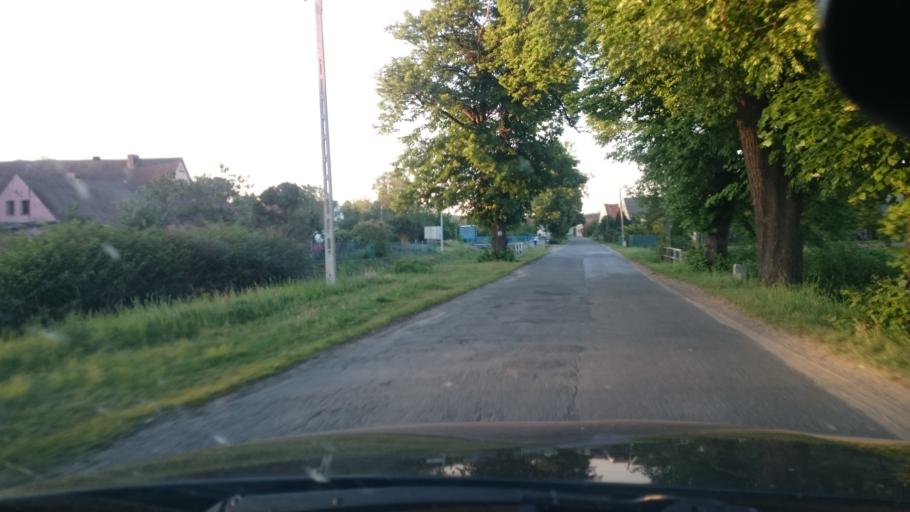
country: PL
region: Lower Silesian Voivodeship
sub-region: Powiat zabkowicki
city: Kamieniec Zabkowicki
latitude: 50.4920
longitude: 16.8270
